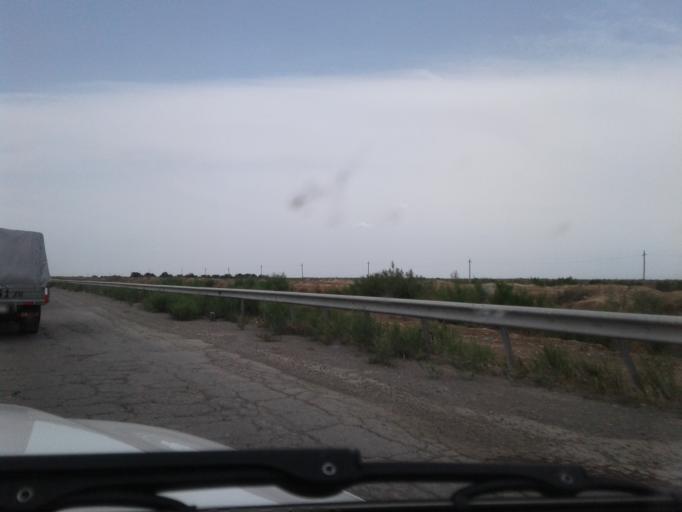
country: TM
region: Ahal
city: Tejen
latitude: 37.2915
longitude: 60.7955
